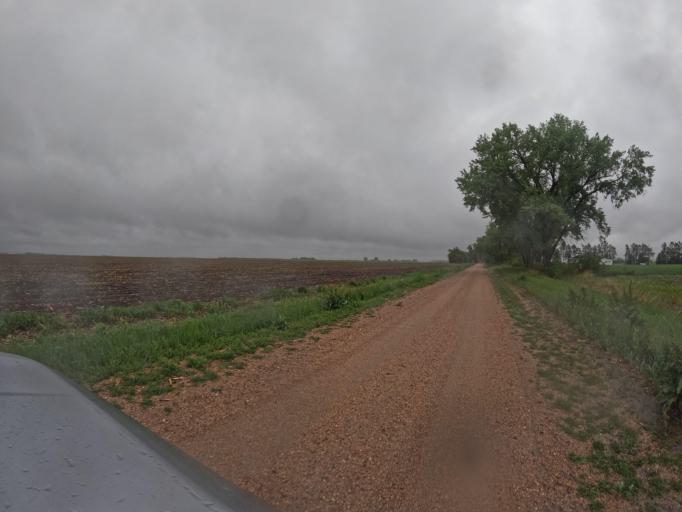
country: US
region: Nebraska
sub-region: Clay County
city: Harvard
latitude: 40.6238
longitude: -98.1040
